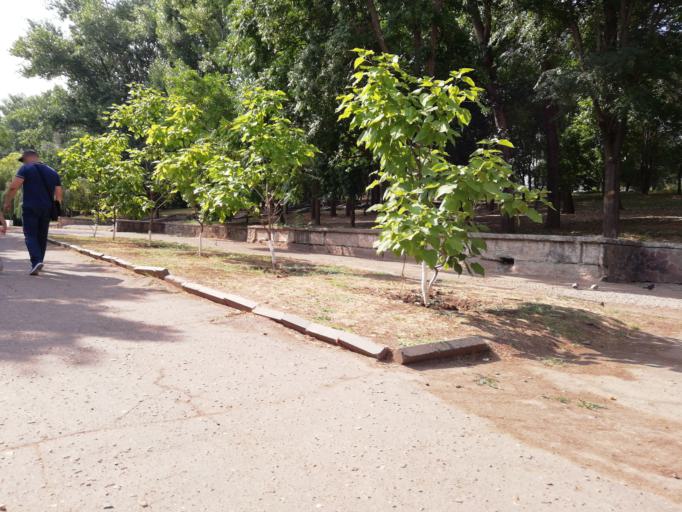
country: RU
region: Rostov
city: Severnyy
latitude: 47.2774
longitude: 39.7112
